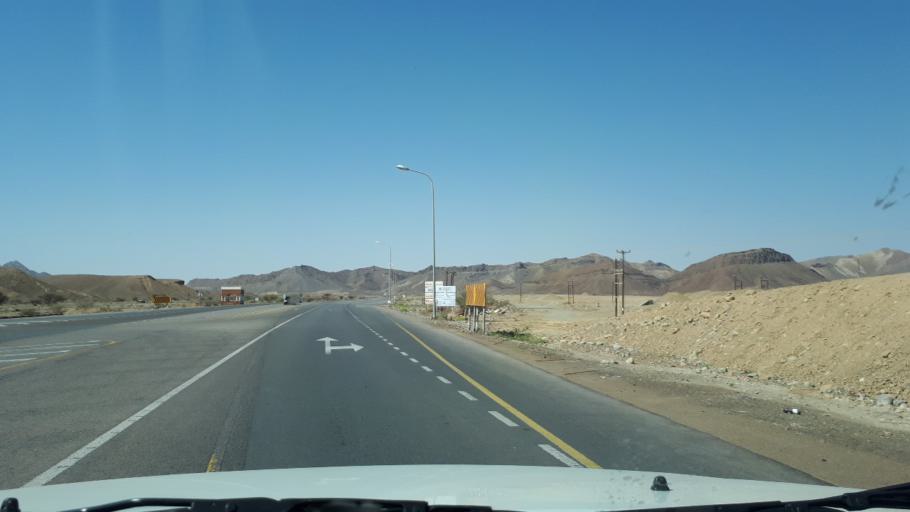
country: OM
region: Ash Sharqiyah
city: Sur
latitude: 22.3743
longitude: 59.3191
